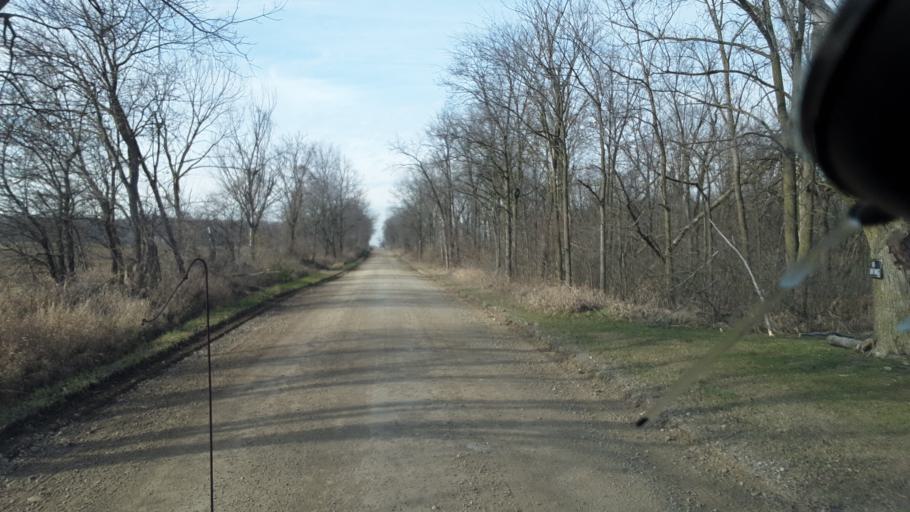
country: US
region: Ohio
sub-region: Defiance County
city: Hicksville
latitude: 41.2700
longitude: -84.8516
